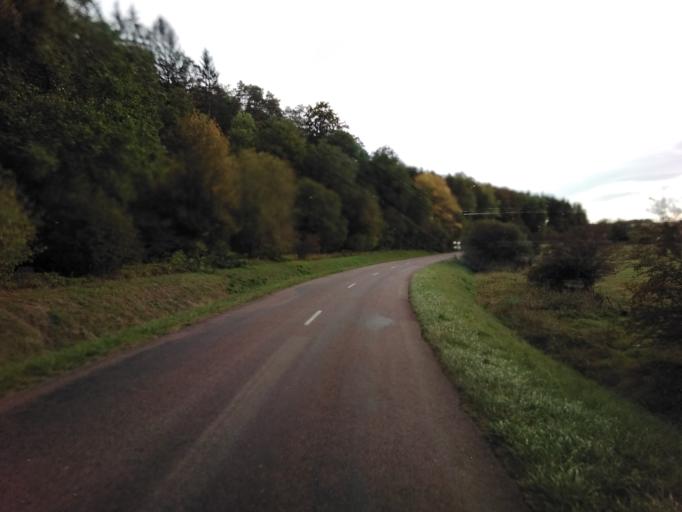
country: FR
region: Champagne-Ardenne
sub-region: Departement de l'Aube
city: Les Riceys
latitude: 47.9316
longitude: 4.3553
